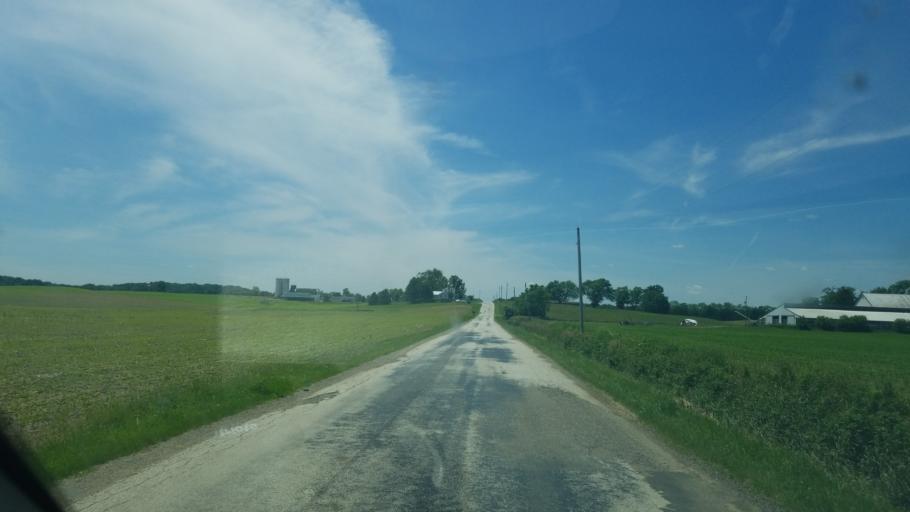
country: US
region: Ohio
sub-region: Stark County
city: Alliance
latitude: 40.8577
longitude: -81.0580
